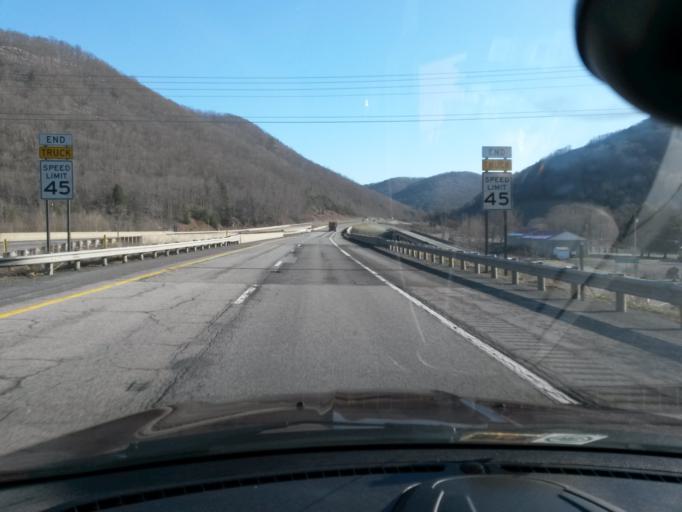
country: US
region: West Virginia
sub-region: Braxton County
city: Sutton
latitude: 38.4988
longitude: -80.7564
